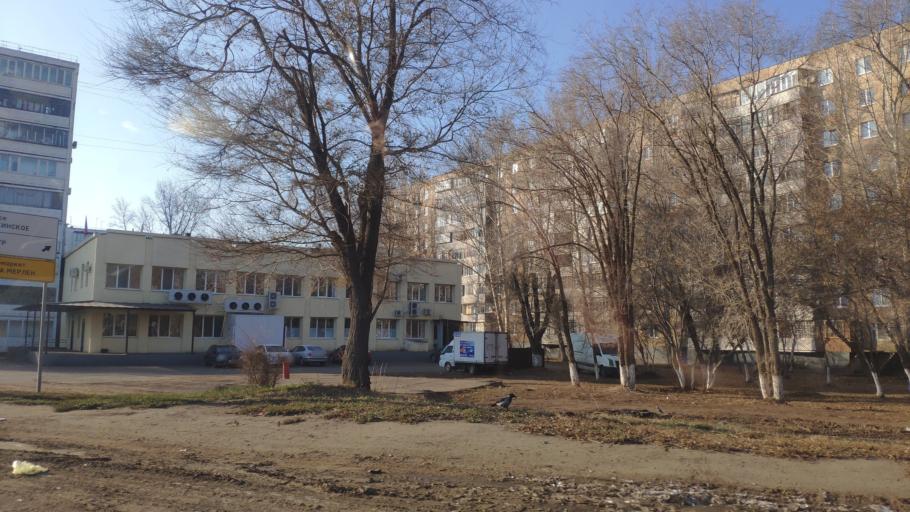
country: RU
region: Orenburg
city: Prigorodnyy
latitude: 51.7777
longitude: 55.1909
